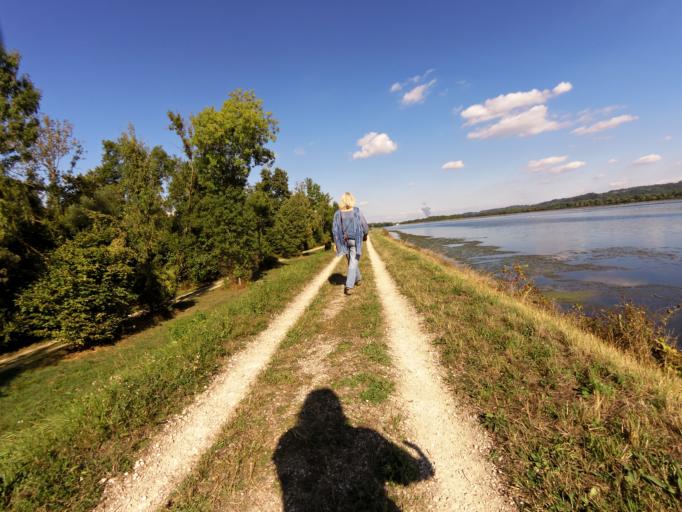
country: DE
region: Bavaria
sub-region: Lower Bavaria
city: Ergolding
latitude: 48.5729
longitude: 12.1970
